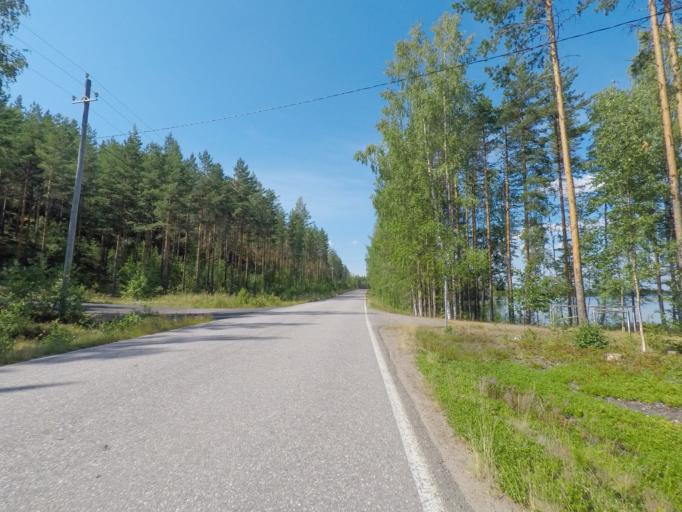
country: FI
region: Southern Savonia
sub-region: Mikkeli
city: Puumala
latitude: 61.4632
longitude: 28.1727
